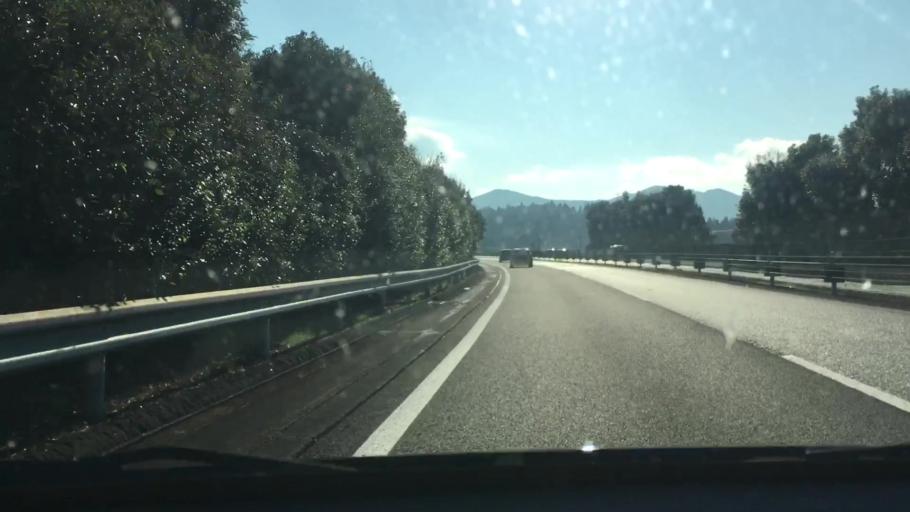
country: JP
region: Kagoshima
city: Okuchi-shinohara
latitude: 32.0124
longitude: 130.7581
